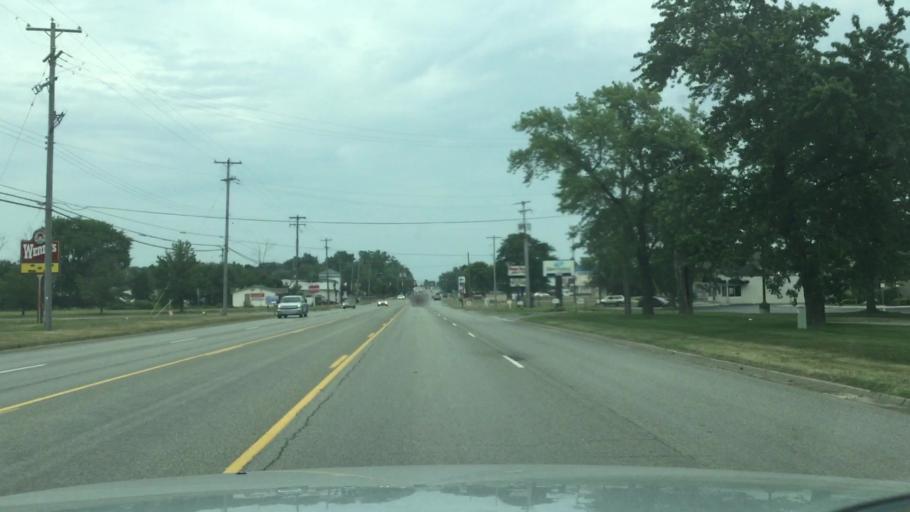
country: US
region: Michigan
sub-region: Genesee County
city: Grand Blanc
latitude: 42.9442
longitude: -83.6964
